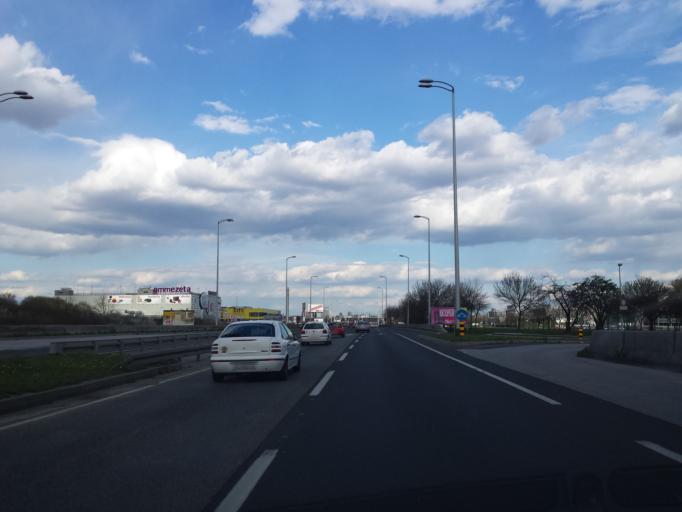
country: HR
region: Grad Zagreb
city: Dubrava
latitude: 45.7991
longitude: 16.0435
